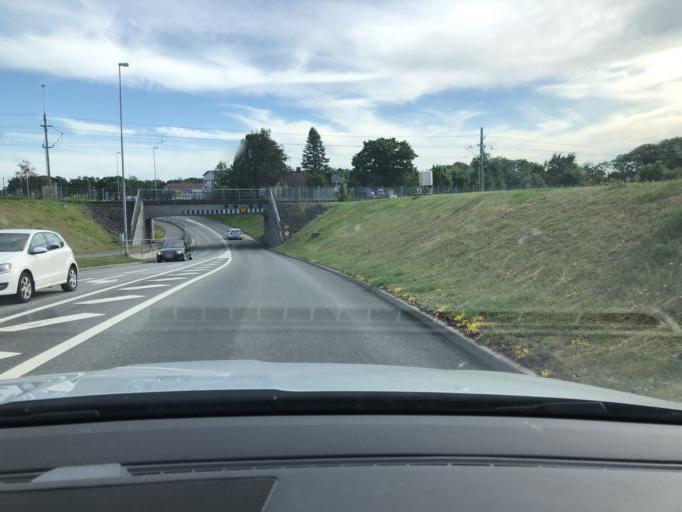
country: SE
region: Skane
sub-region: Bromolla Kommun
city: Bromoella
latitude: 56.0681
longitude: 14.4771
